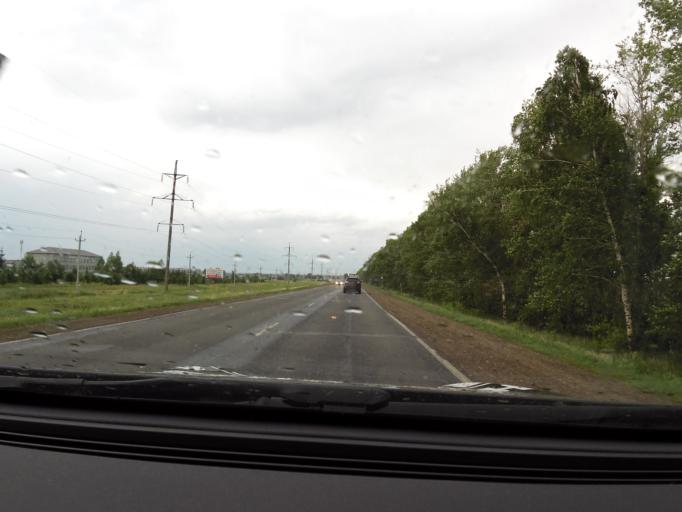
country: RU
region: Bashkortostan
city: Mikhaylovka
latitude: 54.8610
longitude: 55.7554
